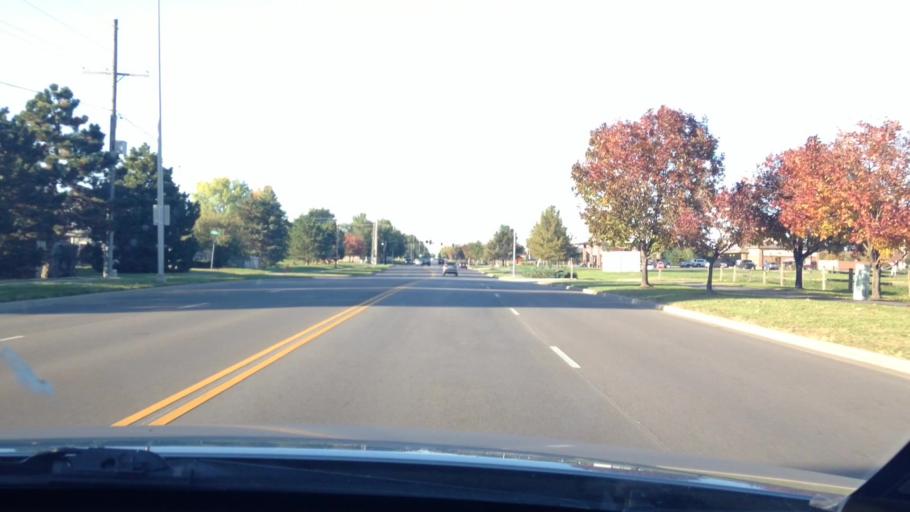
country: US
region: Kansas
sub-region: Johnson County
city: Gardner
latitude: 38.7941
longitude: -94.9276
